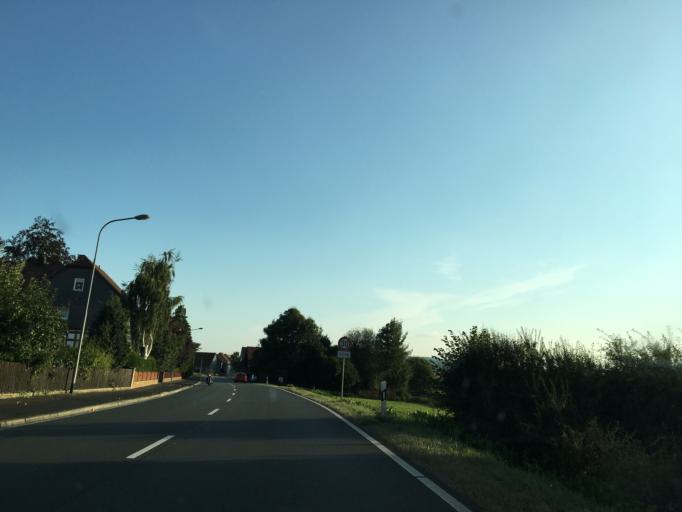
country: DE
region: Hesse
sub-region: Regierungsbezirk Giessen
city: Munchhausen
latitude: 50.9302
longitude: 8.7049
